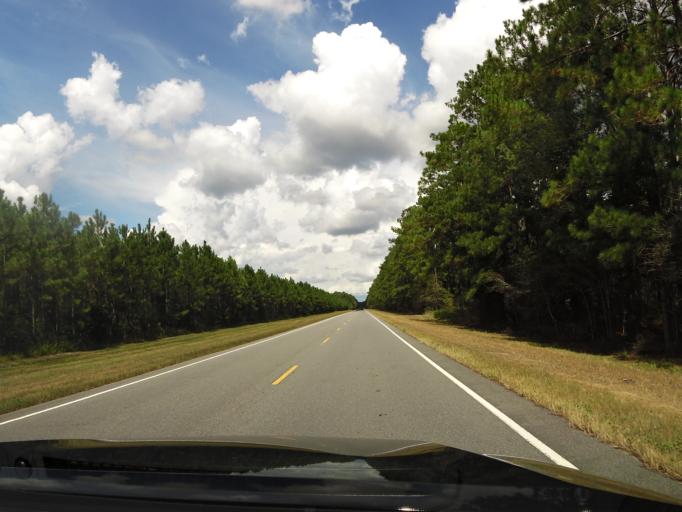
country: US
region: Georgia
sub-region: Charlton County
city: Folkston
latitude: 30.9933
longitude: -82.0262
